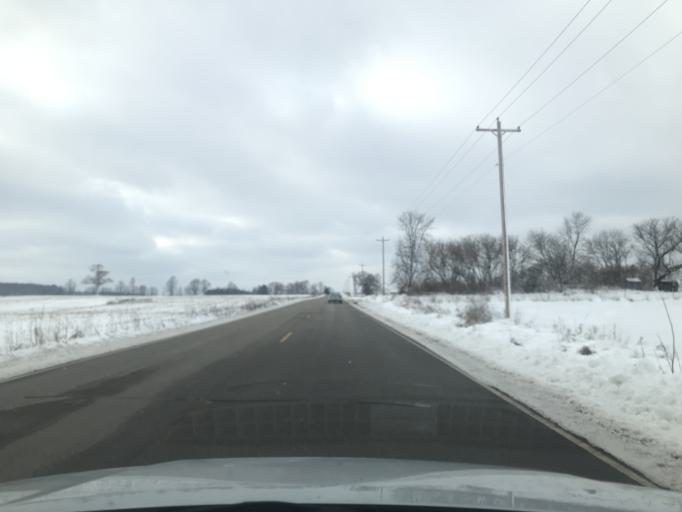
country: US
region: Wisconsin
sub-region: Oconto County
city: Oconto
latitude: 44.9499
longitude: -87.9077
